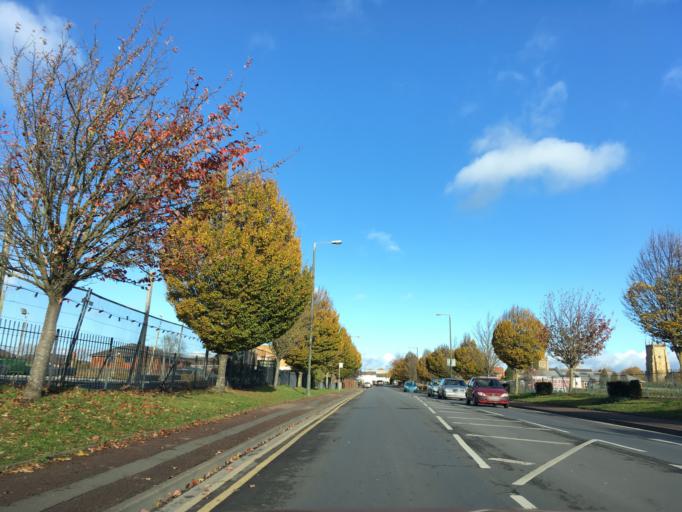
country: GB
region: England
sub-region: Worcestershire
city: Evesham
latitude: 52.0884
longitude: -1.9513
